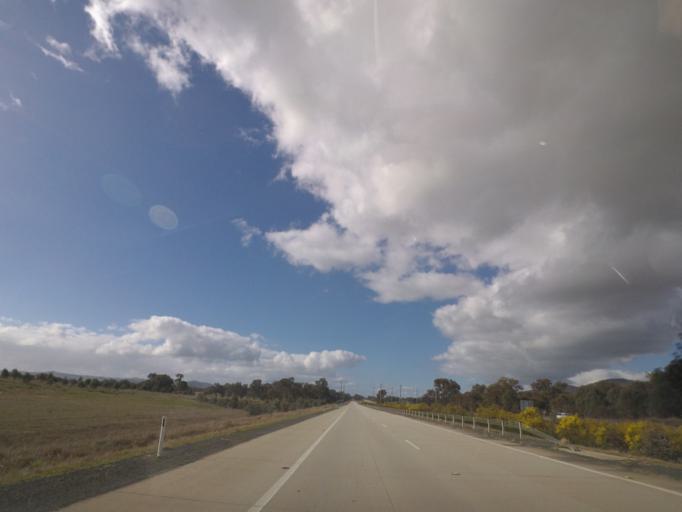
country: AU
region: New South Wales
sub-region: Greater Hume Shire
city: Holbrook
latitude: -35.6975
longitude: 147.3383
